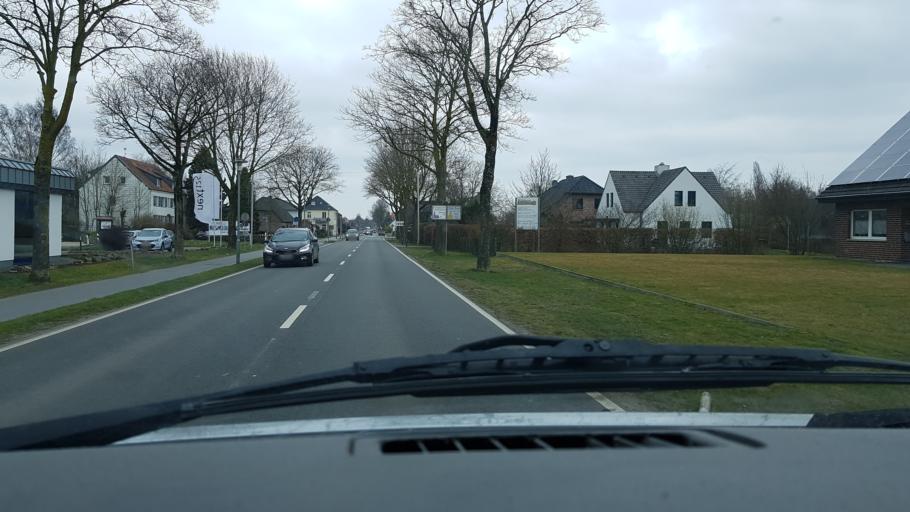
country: DE
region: North Rhine-Westphalia
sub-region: Regierungsbezirk Dusseldorf
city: Kranenburg
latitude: 51.7842
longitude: 6.0209
